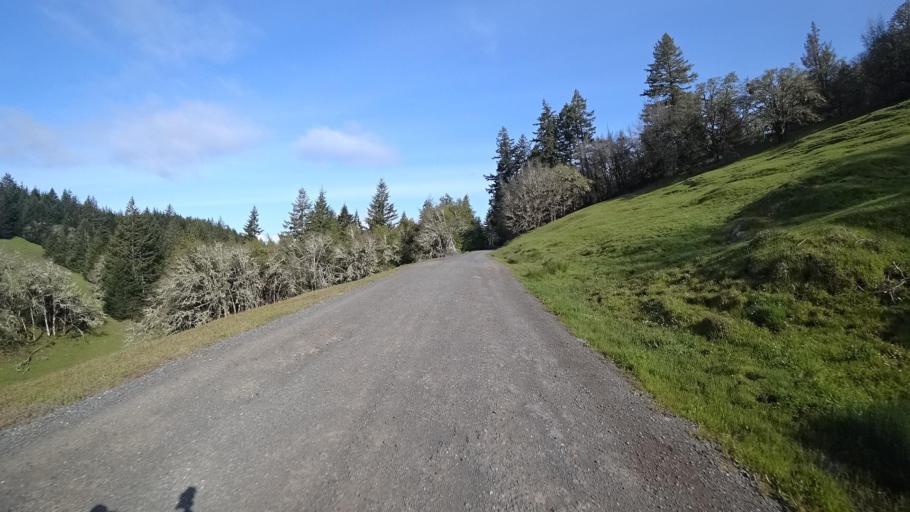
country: US
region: California
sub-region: Humboldt County
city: Hydesville
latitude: 40.6467
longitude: -123.9222
